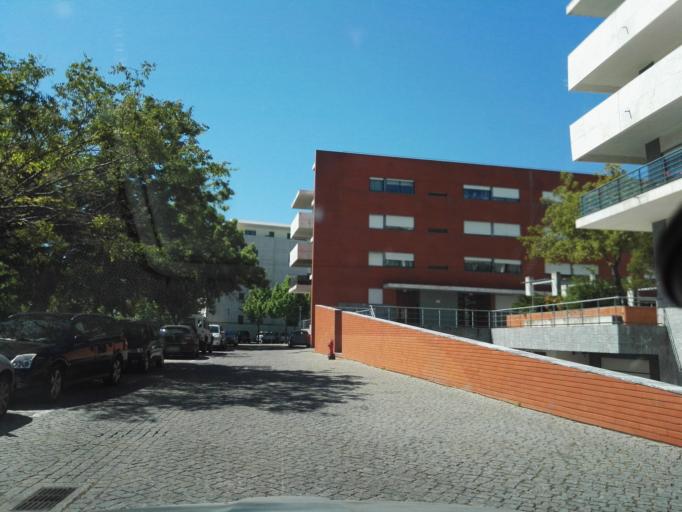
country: PT
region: Lisbon
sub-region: Loures
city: Moscavide
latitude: 38.7824
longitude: -9.0936
